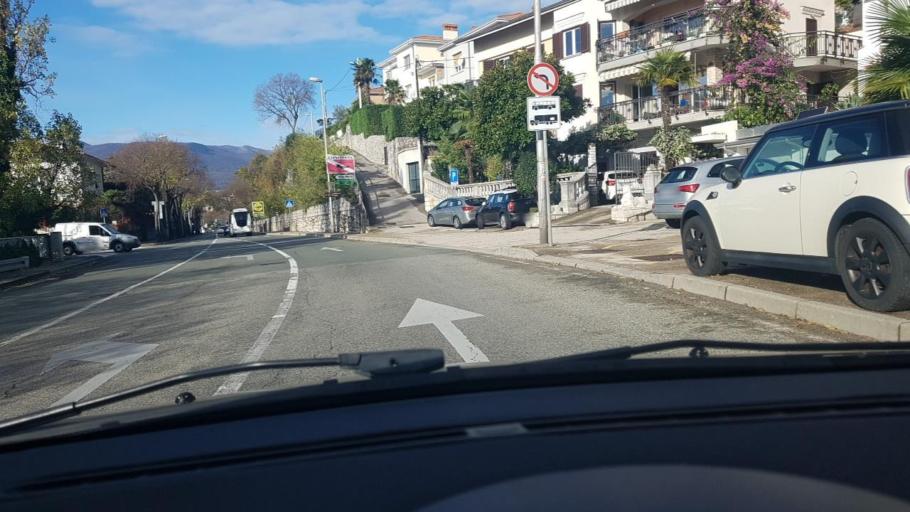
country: HR
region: Primorsko-Goranska
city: Marinici
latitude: 45.3407
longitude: 14.3768
